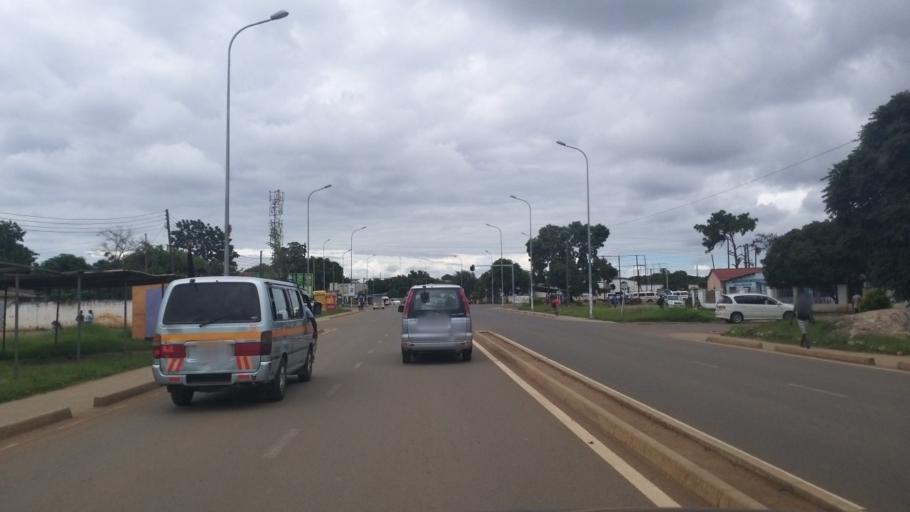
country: ZM
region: Lusaka
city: Lusaka
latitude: -15.4381
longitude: 28.3116
